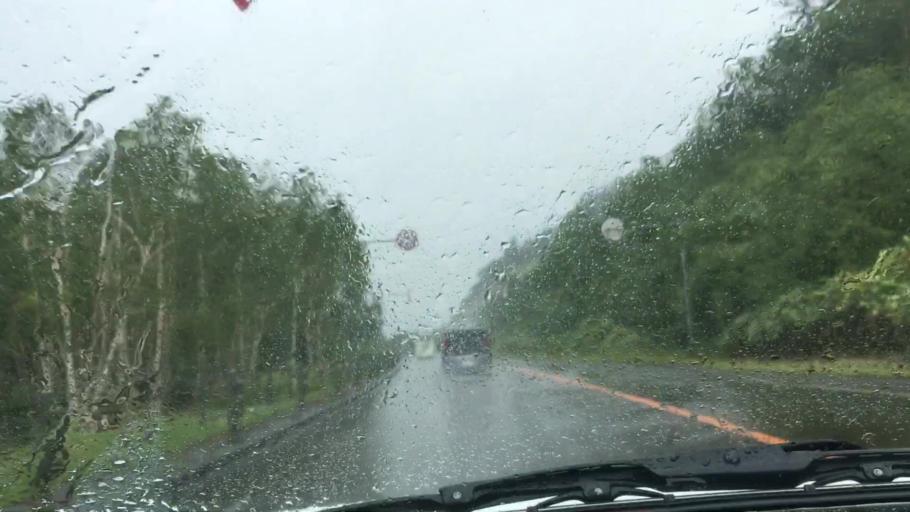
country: JP
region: Hokkaido
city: Sapporo
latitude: 42.8742
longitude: 141.1444
